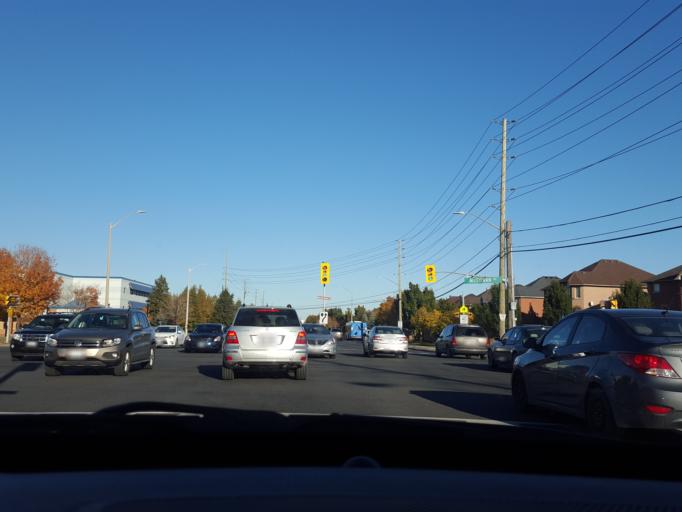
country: CA
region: Ontario
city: Markham
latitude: 43.8492
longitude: -79.2800
